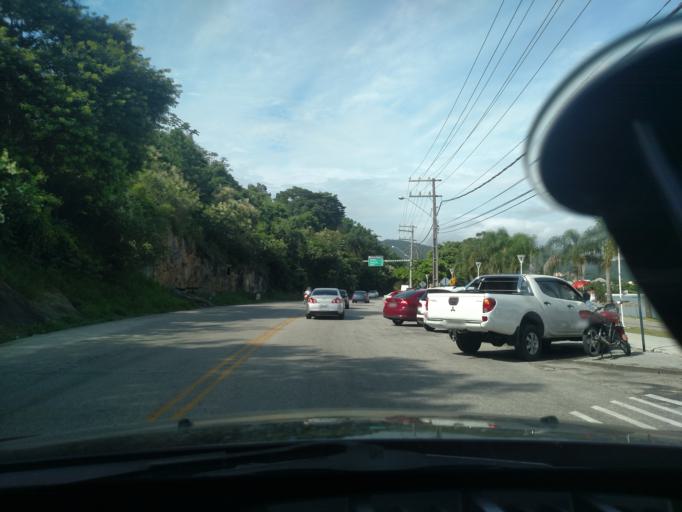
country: BR
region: Santa Catarina
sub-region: Porto Belo
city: Porto Belo
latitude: -27.1486
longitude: -48.5351
